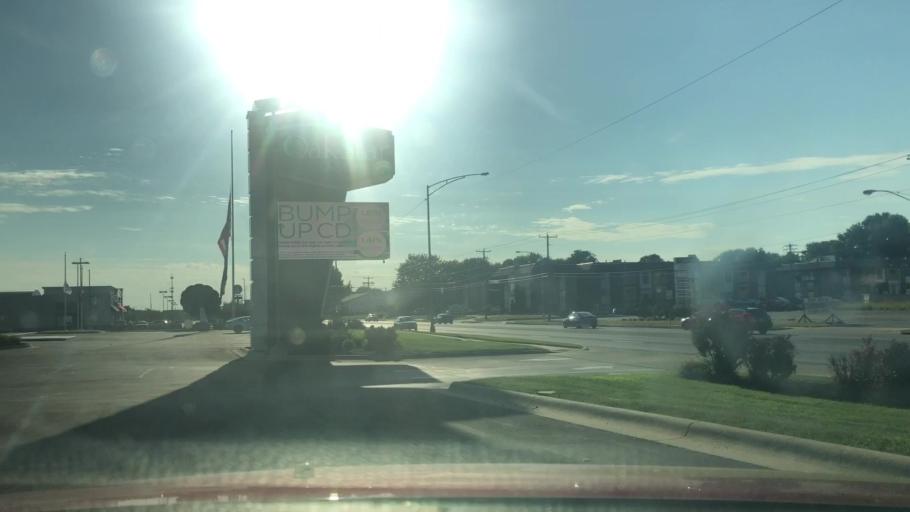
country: US
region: Missouri
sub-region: Greene County
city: Springfield
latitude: 37.1595
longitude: -93.2799
